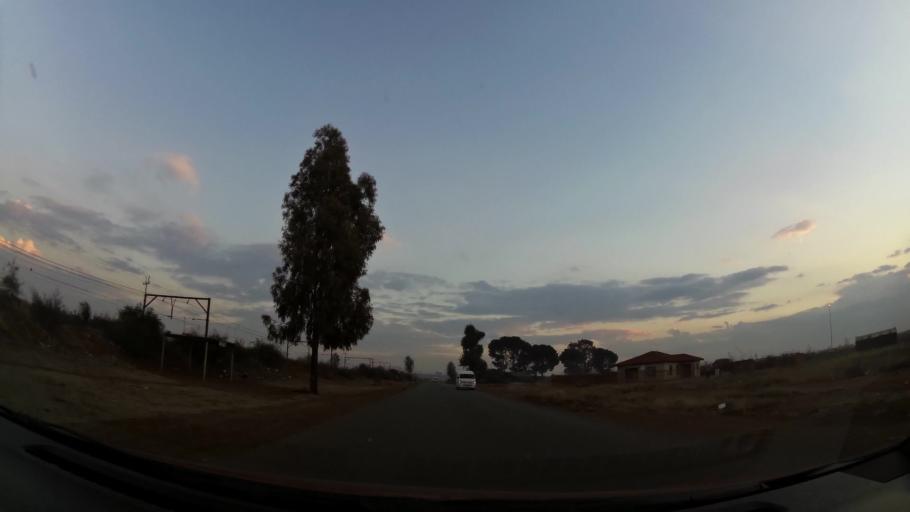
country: ZA
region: Gauteng
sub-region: City of Johannesburg Metropolitan Municipality
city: Orange Farm
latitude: -26.5537
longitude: 27.8810
